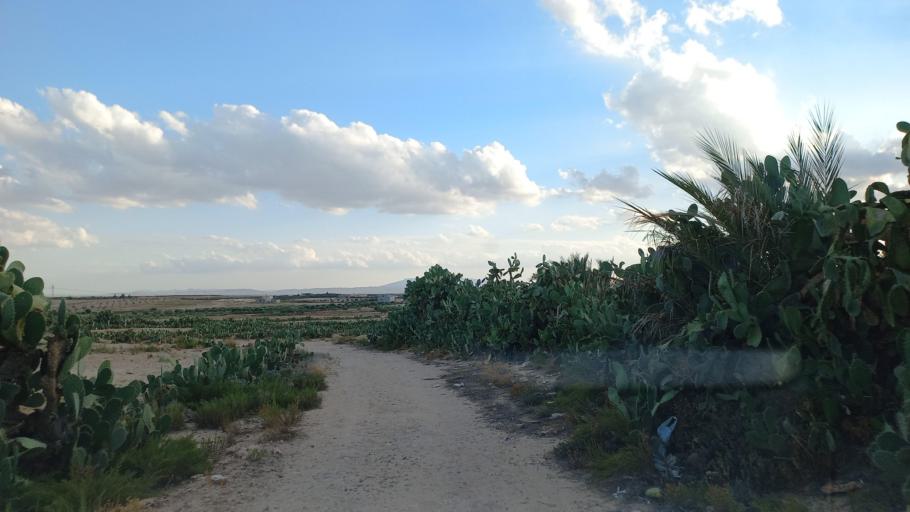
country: TN
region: Al Qasrayn
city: Sbiba
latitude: 35.3888
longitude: 9.0451
